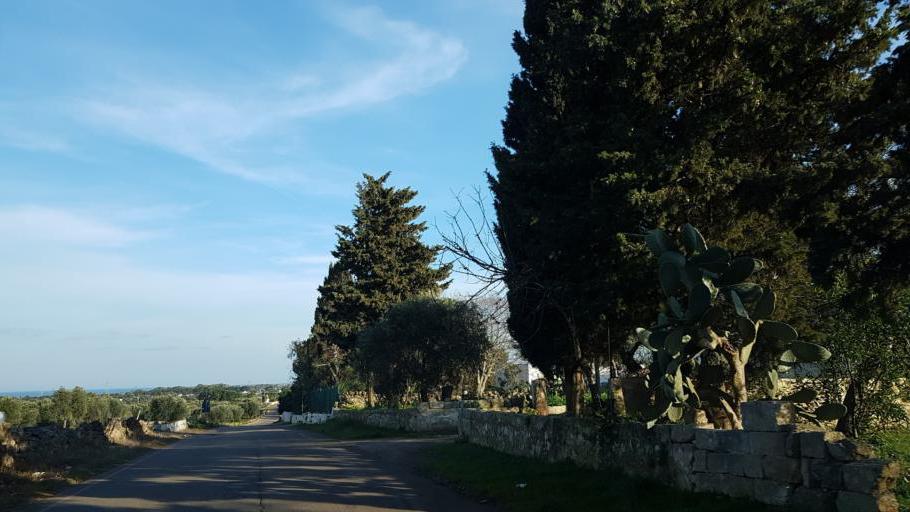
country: IT
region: Apulia
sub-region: Provincia di Brindisi
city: San Vito dei Normanni
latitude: 40.6967
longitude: 17.7426
